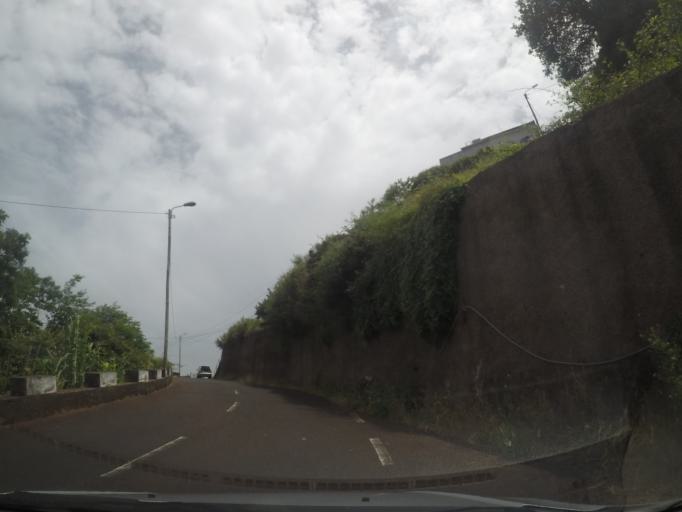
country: PT
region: Madeira
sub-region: Santa Cruz
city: Camacha
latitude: 32.6812
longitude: -16.8429
